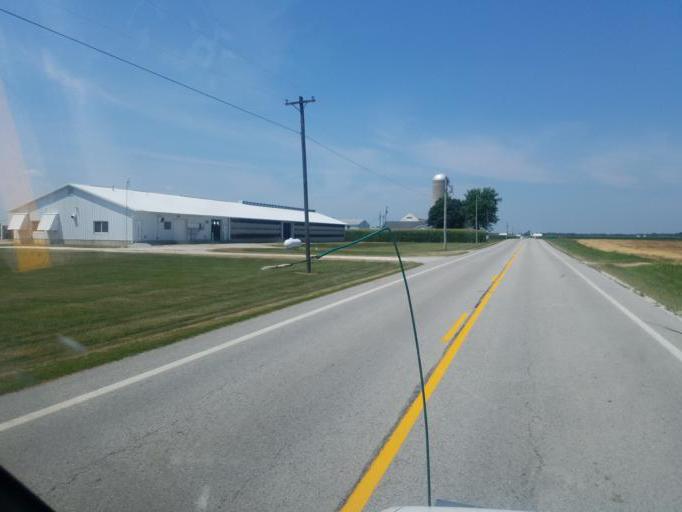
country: US
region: Ohio
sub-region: Auglaize County
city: New Bremen
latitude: 40.4575
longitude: -84.4341
